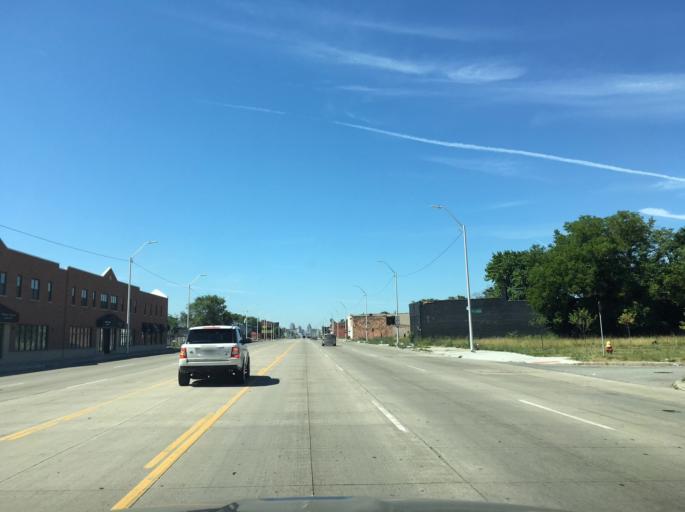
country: US
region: Michigan
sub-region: Wayne County
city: Hamtramck
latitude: 42.3882
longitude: -83.0085
